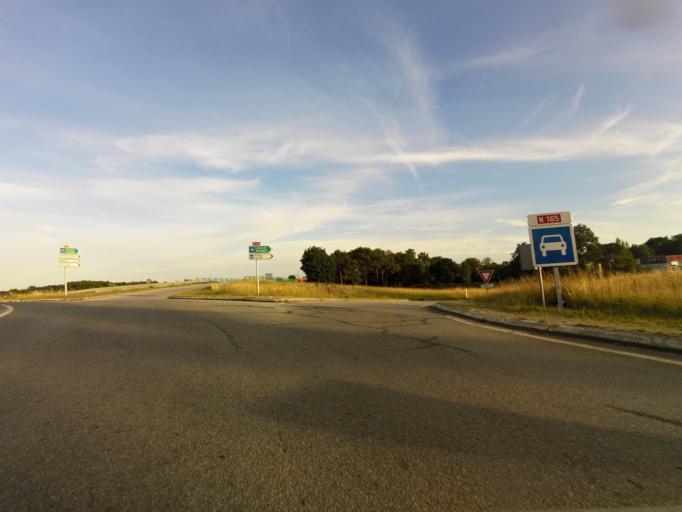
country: FR
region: Brittany
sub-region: Departement du Morbihan
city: Ploeren
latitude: 47.6616
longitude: -2.8605
